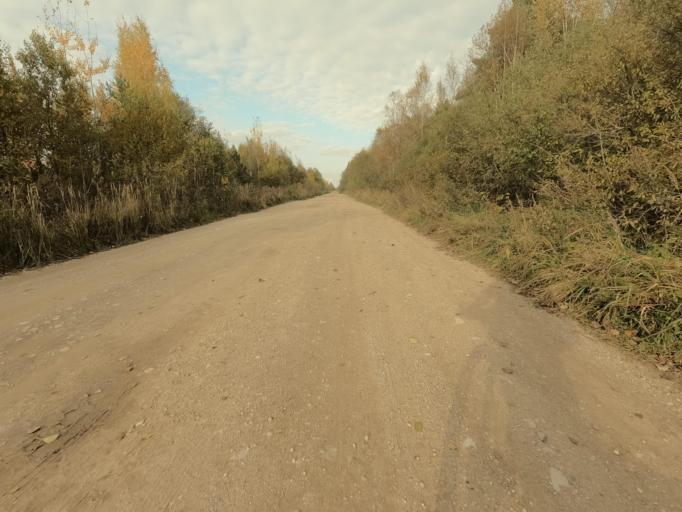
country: RU
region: Novgorod
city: Volkhovskiy
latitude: 58.9090
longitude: 31.0386
